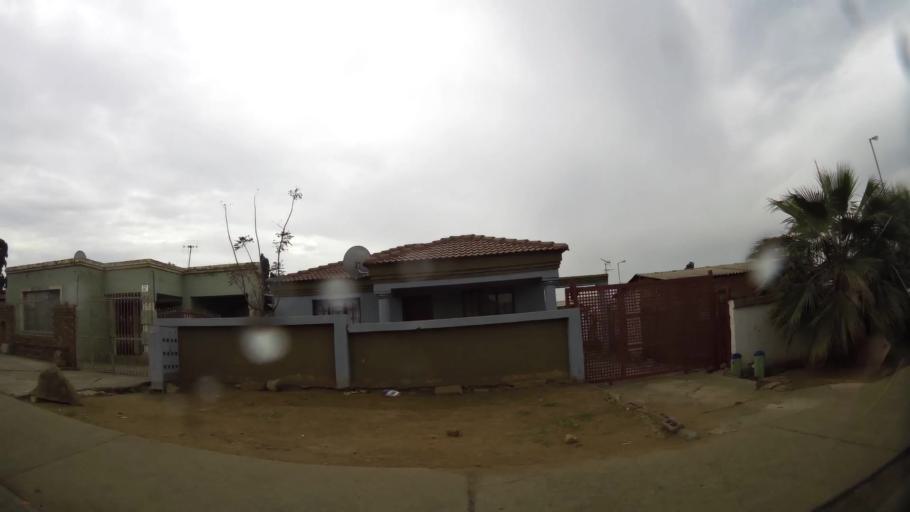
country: ZA
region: Gauteng
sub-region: City of Tshwane Metropolitan Municipality
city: Pretoria
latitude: -25.7162
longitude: 28.3558
